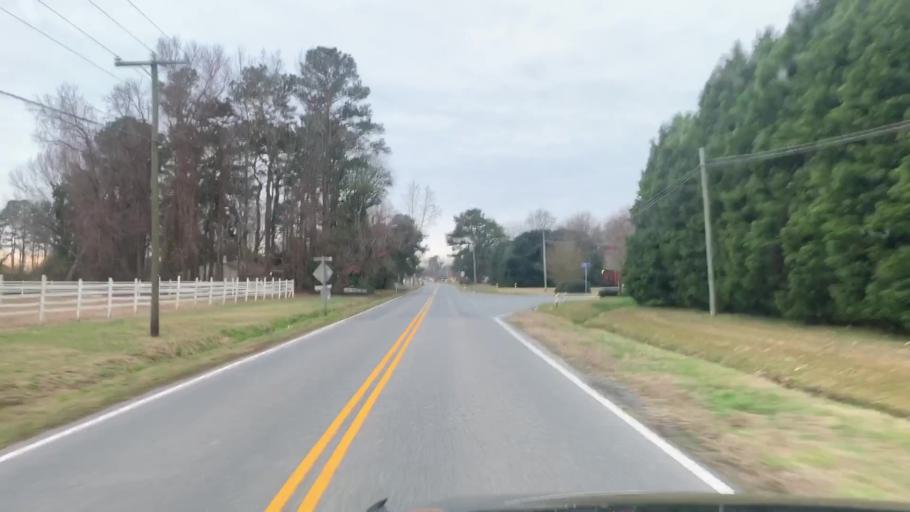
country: US
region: North Carolina
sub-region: Currituck County
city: Moyock
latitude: 36.6389
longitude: -76.2052
